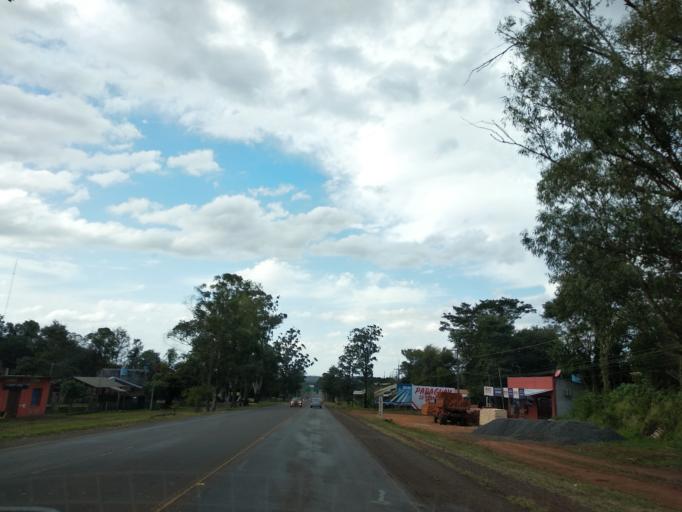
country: PY
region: Itapua
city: San Juan del Parana
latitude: -27.2930
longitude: -55.9284
